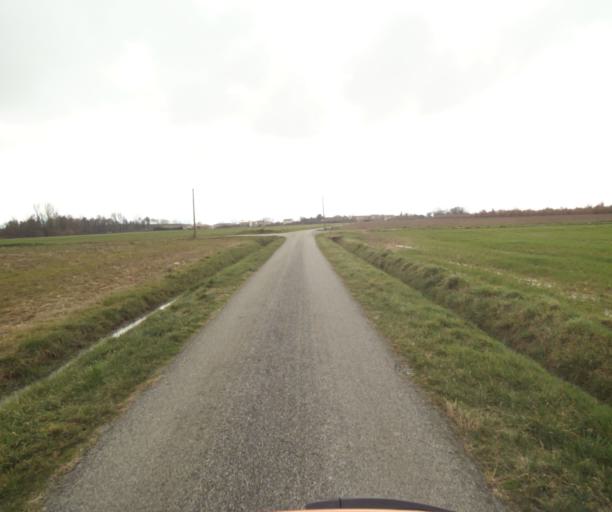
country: FR
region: Languedoc-Roussillon
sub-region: Departement de l'Aude
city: Belpech
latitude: 43.1744
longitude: 1.6911
